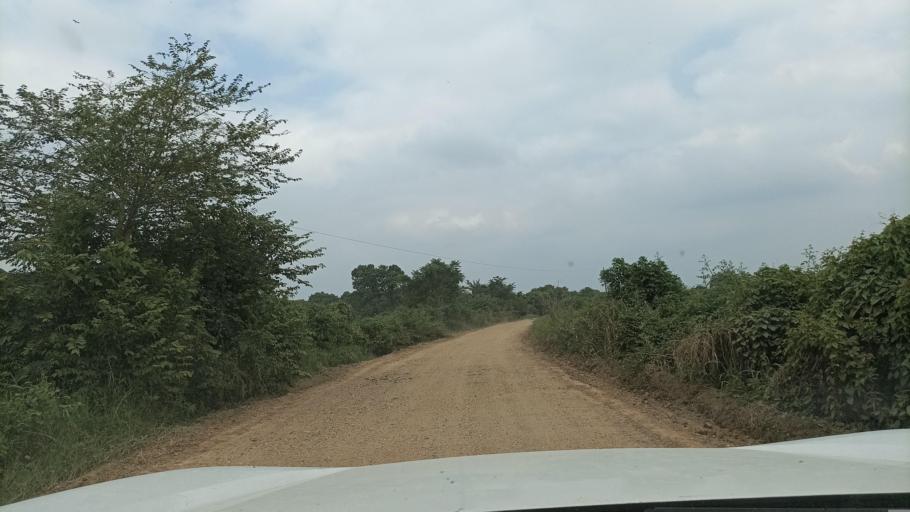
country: MX
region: Veracruz
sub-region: Texistepec
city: San Lorenzo Tenochtitlan
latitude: 17.7814
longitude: -94.7908
